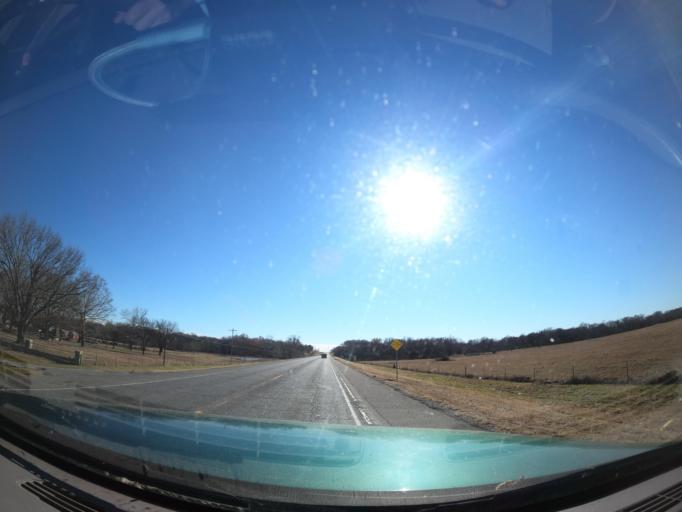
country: US
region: Oklahoma
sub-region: Muskogee County
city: Haskell
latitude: 35.8456
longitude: -95.6775
